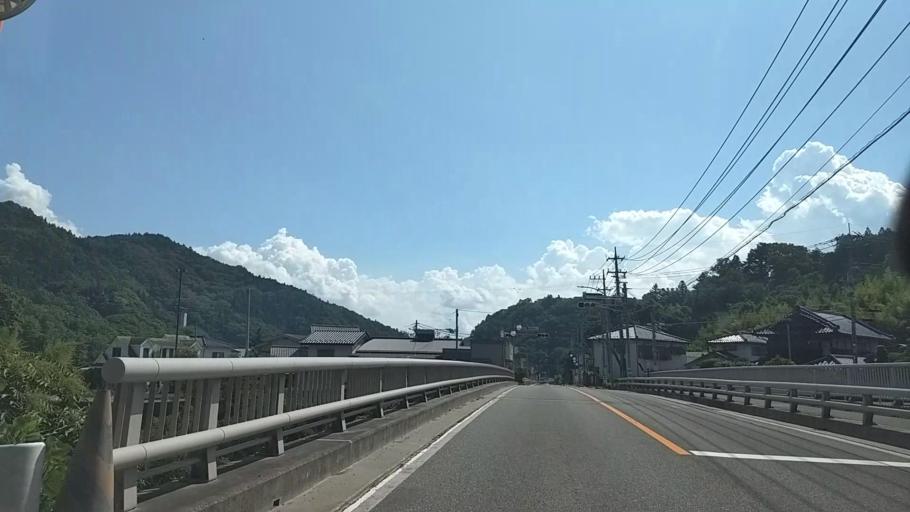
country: JP
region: Yamanashi
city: Ryuo
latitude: 35.4764
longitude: 138.4447
